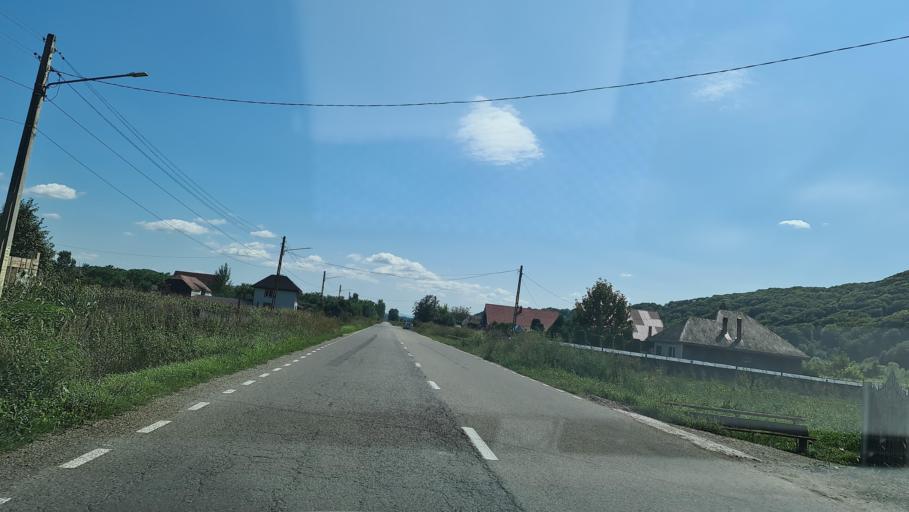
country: RO
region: Neamt
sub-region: Comuna Tazlau
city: Tazlau
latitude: 46.7083
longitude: 26.4877
